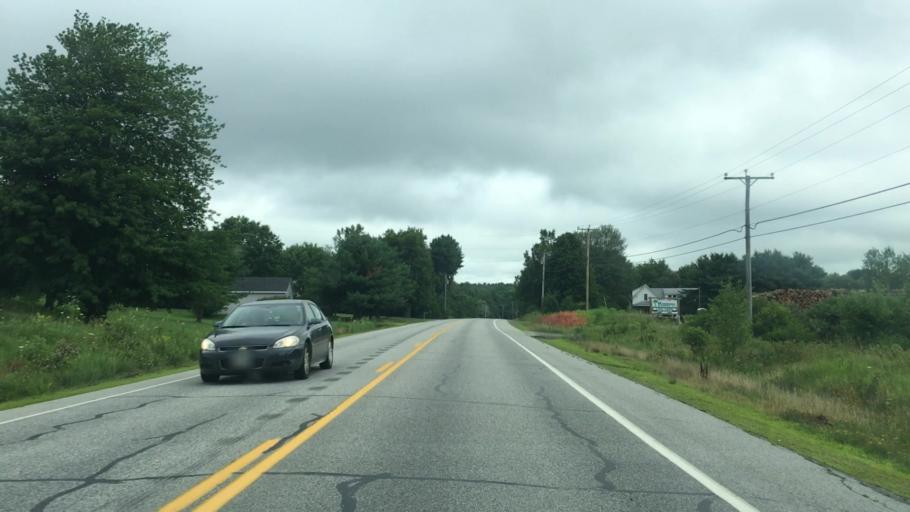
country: US
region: Maine
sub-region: Kennebec County
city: Pittston
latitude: 44.1595
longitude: -69.7450
